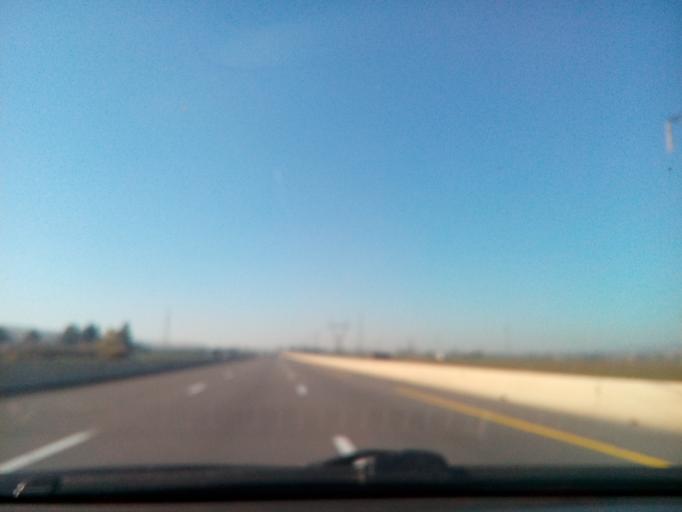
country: DZ
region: Chlef
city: Boukadir
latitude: 36.0473
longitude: 1.1061
